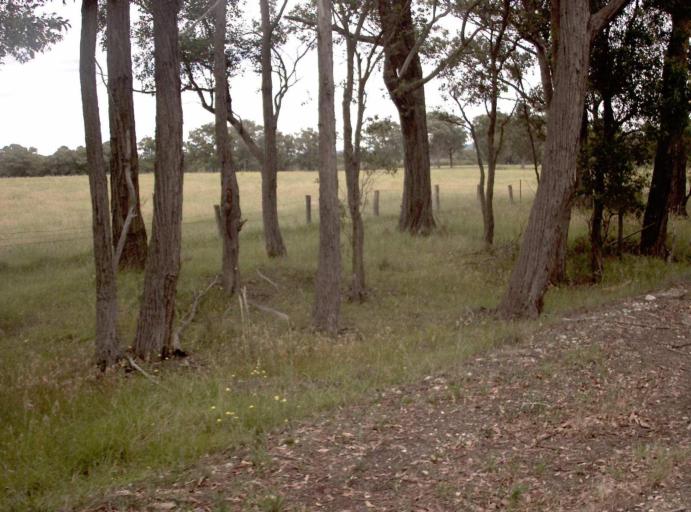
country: AU
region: Victoria
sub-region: East Gippsland
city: Bairnsdale
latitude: -37.7866
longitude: 147.3245
